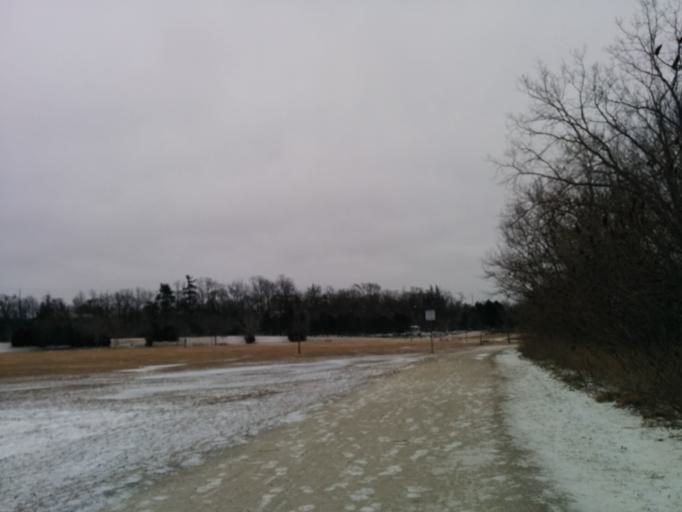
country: CA
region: Ontario
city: Mississauga
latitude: 43.5492
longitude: -79.6548
